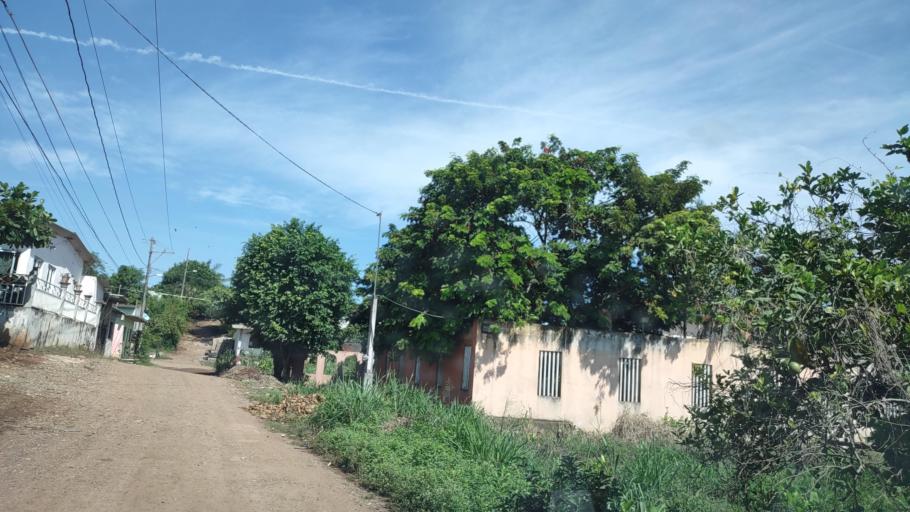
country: MX
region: Veracruz
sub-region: Martinez de la Torre
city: La Union Paso Largo
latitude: 20.1273
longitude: -96.9930
